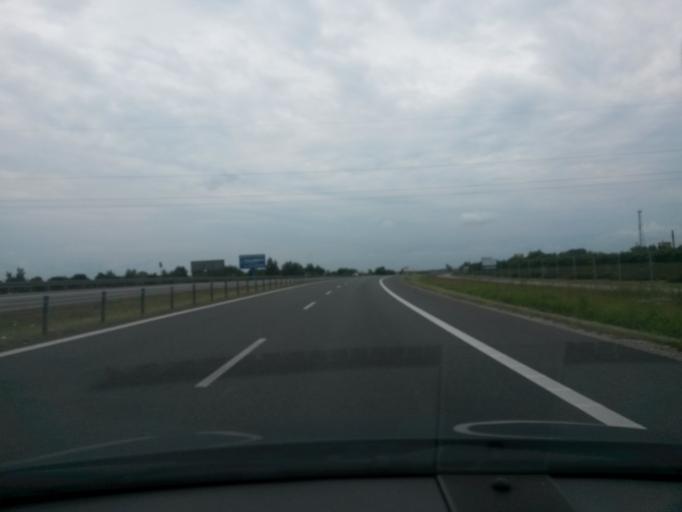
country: PL
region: Masovian Voivodeship
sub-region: Powiat zyrardowski
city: Mszczonow
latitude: 51.9851
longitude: 20.5335
